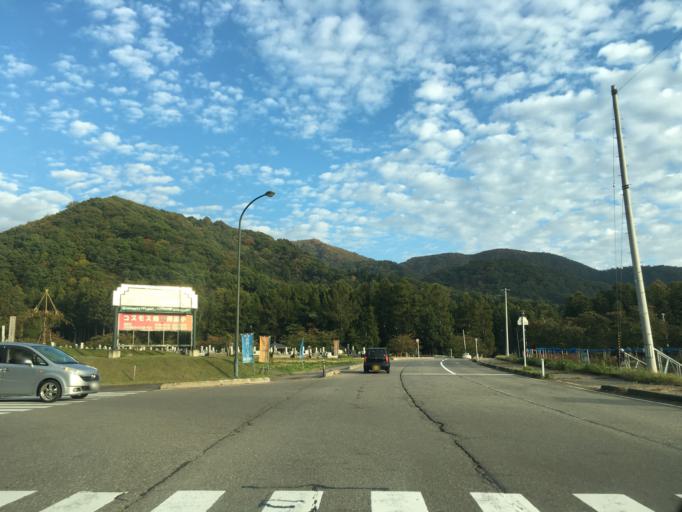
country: JP
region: Fukushima
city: Inawashiro
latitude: 37.5401
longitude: 140.1440
